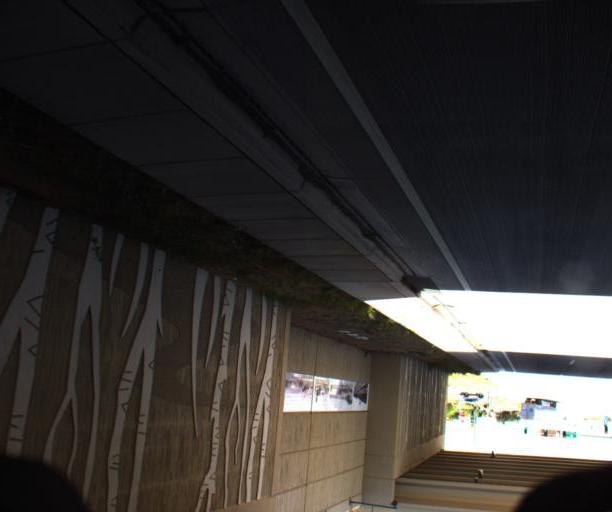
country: US
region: Arizona
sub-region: Cochise County
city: Whetstone
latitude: 31.9645
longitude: -110.3467
